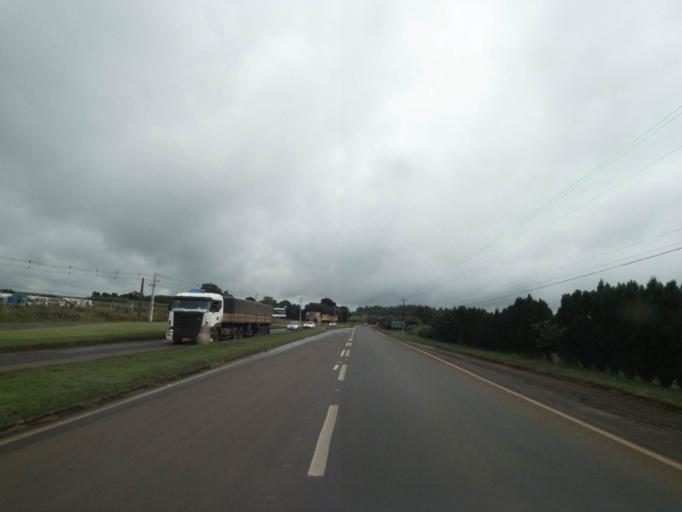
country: BR
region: Parana
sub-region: Marechal Candido Rondon
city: Marechal Candido Rondon
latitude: -24.5707
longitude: -53.9988
